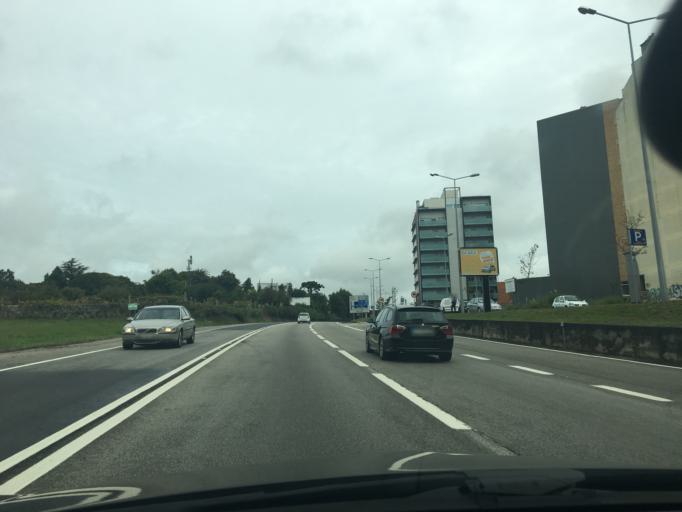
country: PT
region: Porto
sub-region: Maia
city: Maia
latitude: 41.2341
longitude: -8.6270
